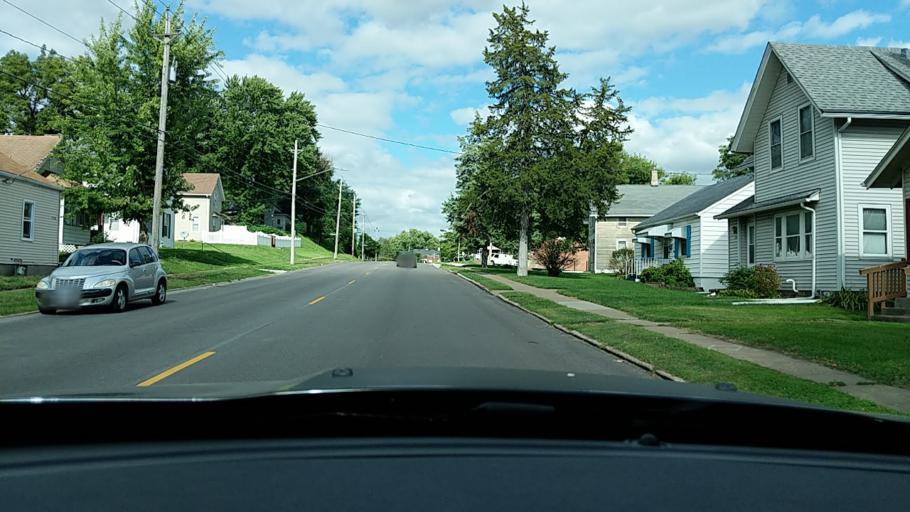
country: US
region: Illinois
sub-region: Rock Island County
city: Rock Island
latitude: 41.5193
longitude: -90.6210
